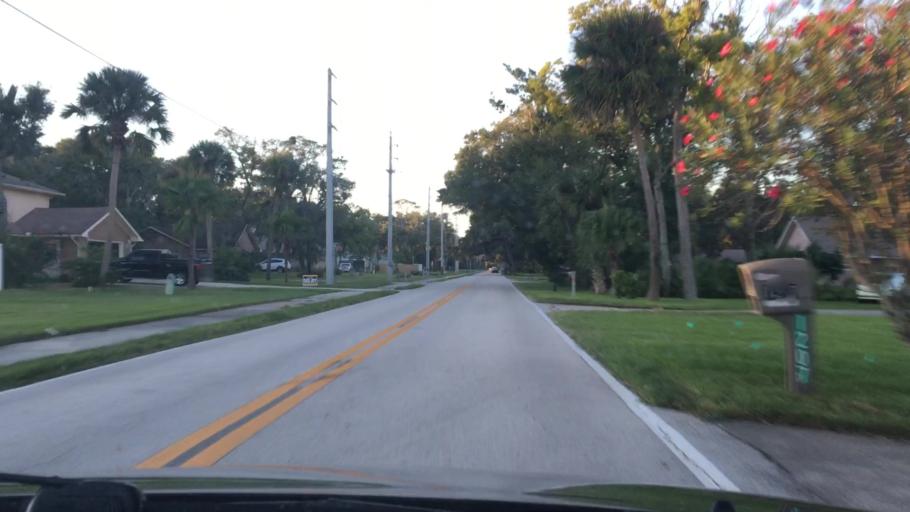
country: US
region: Florida
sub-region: Volusia County
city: Ormond Beach
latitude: 29.3151
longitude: -81.0704
